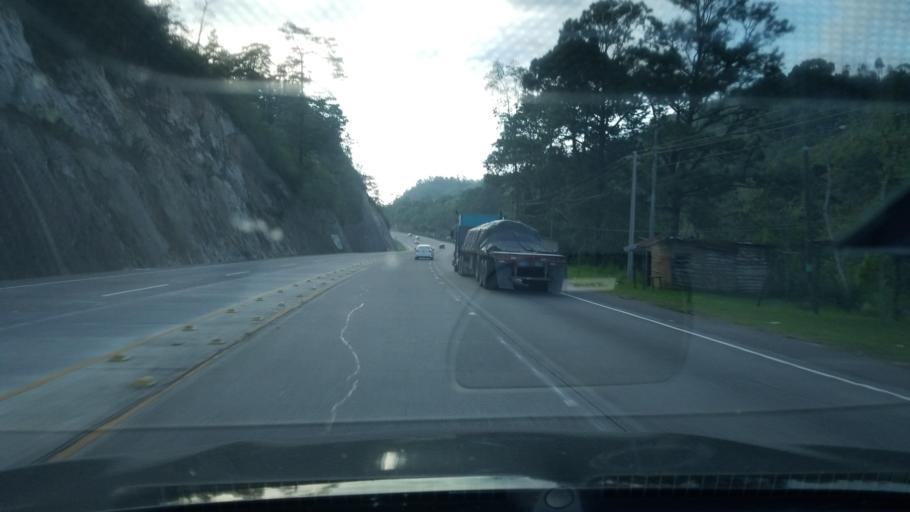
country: HN
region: Comayagua
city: El Socorro
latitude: 14.6567
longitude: -87.9416
